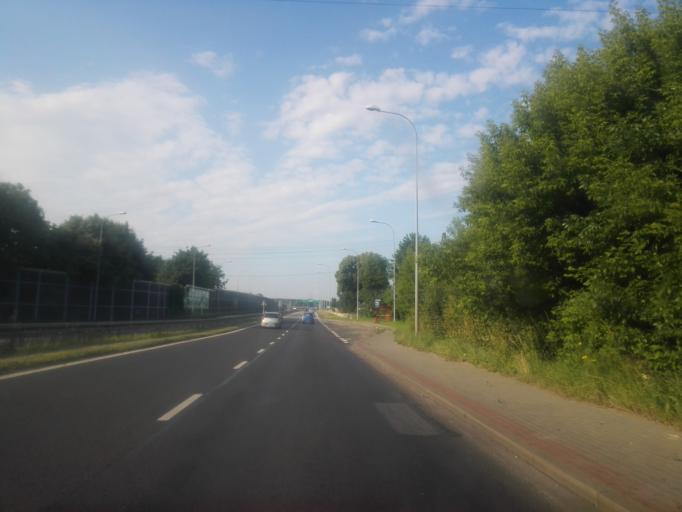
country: PL
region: Silesian Voivodeship
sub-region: Powiat bedzinski
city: Siewierz
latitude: 50.4127
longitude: 19.2046
